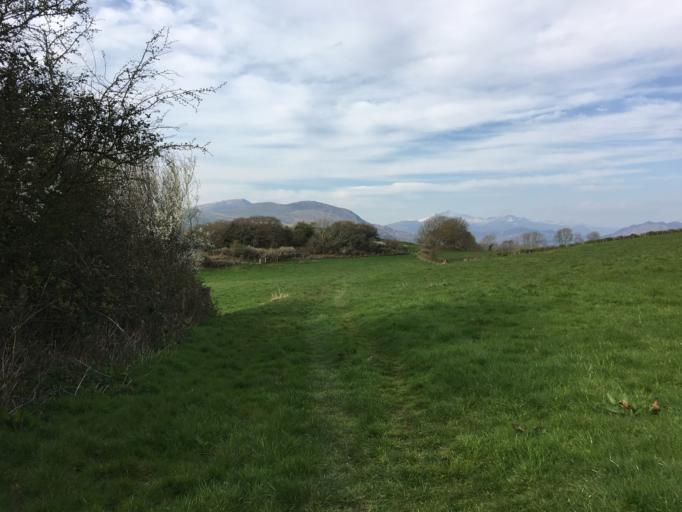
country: GB
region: Wales
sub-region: Gwynedd
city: Porthmadog
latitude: 52.9160
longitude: -4.1050
